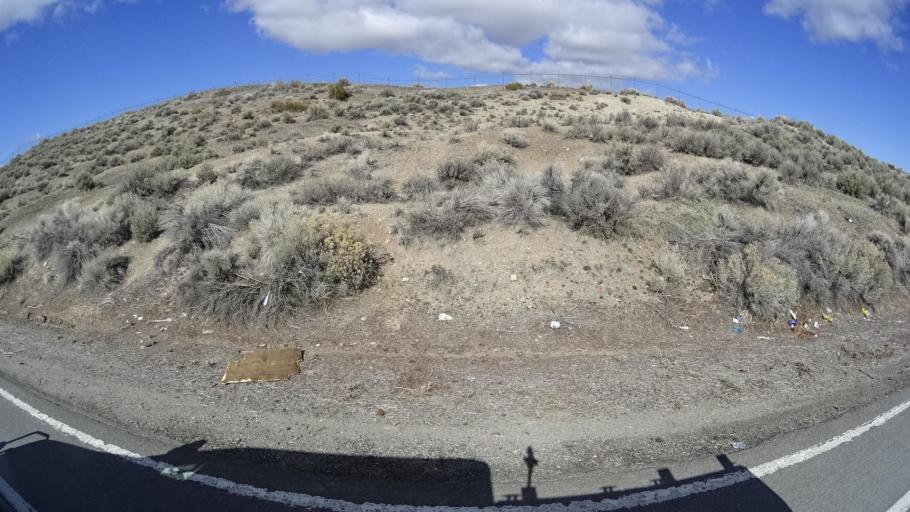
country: US
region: Nevada
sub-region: Washoe County
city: Lemmon Valley
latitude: 39.6639
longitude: -119.8602
